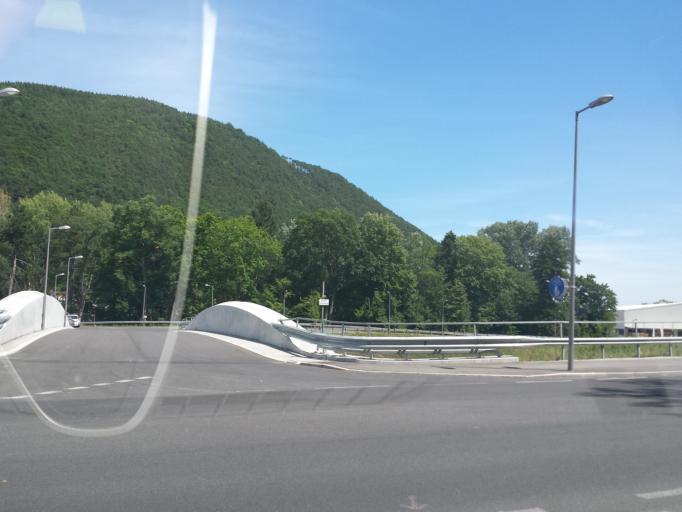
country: AT
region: Lower Austria
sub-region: Politischer Bezirk Neunkirchen
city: Gloggnitz
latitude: 47.6751
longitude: 15.9269
